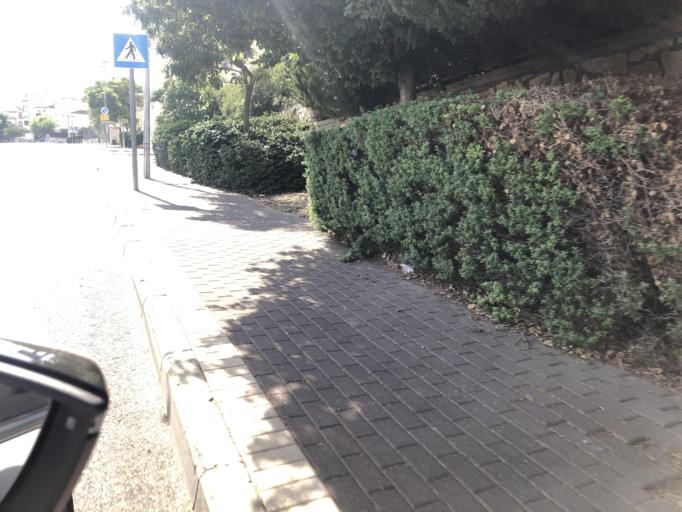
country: IL
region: Haifa
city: Daliyat el Karmil
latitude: 32.6381
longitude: 35.0923
